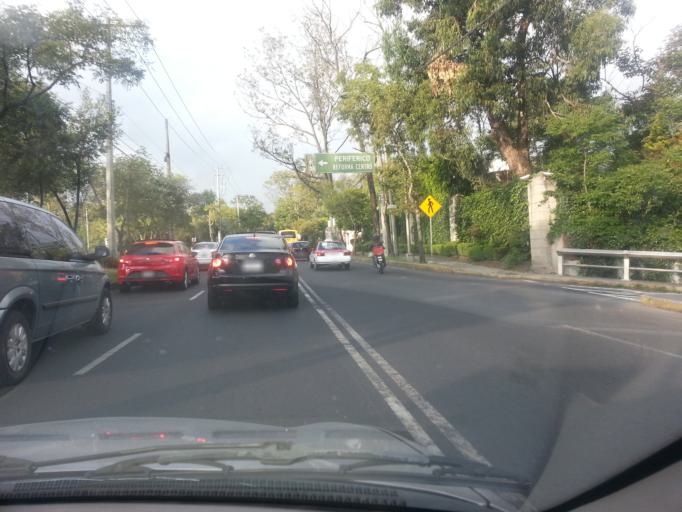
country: MX
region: Mexico City
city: Polanco
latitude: 19.4050
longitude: -99.2294
